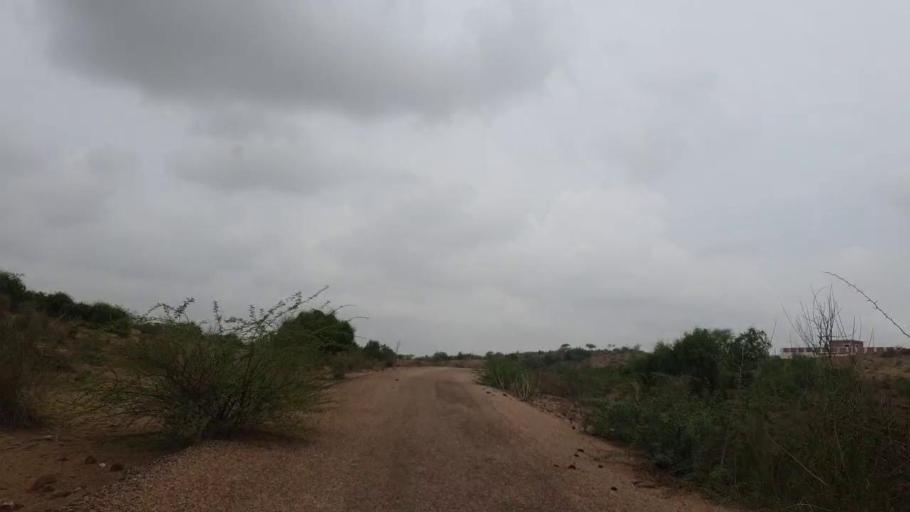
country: PK
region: Sindh
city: Diplo
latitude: 24.5120
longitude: 69.4844
